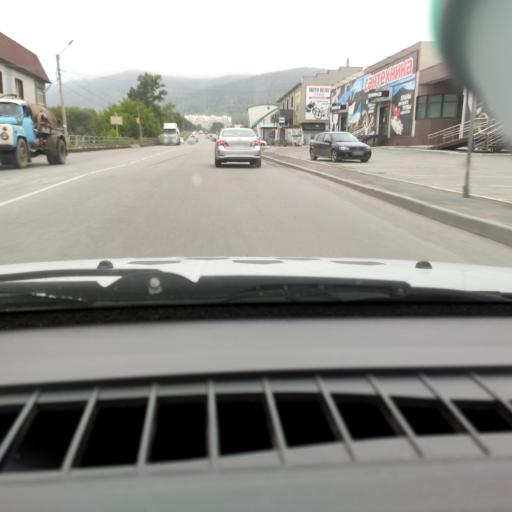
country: RU
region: Chelyabinsk
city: Miass
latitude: 55.0275
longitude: 60.1133
